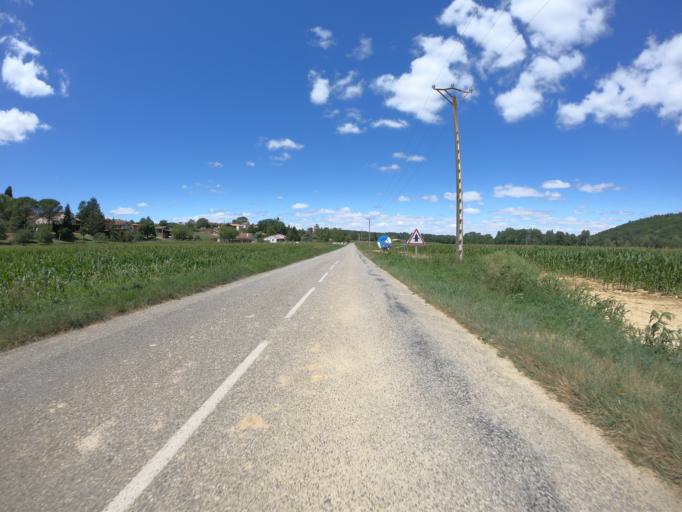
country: FR
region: Midi-Pyrenees
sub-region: Departement de l'Ariege
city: Verniolle
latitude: 43.0608
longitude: 1.7410
